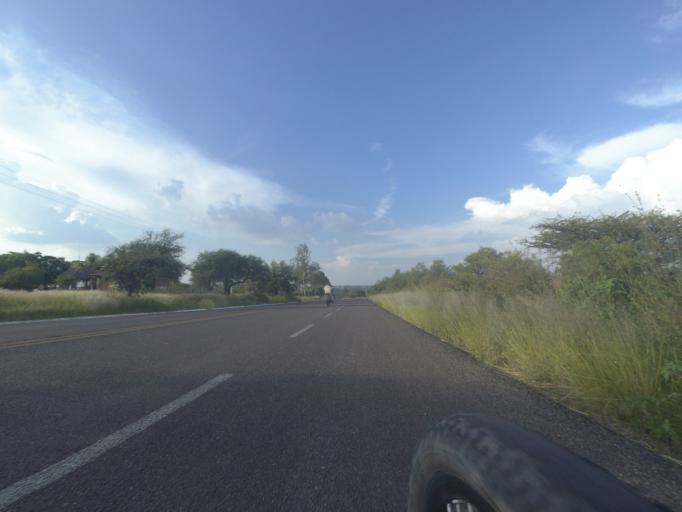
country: MX
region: Aguascalientes
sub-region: Aguascalientes
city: Penuelas (El Cienegal)
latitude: 21.7486
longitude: -102.3508
